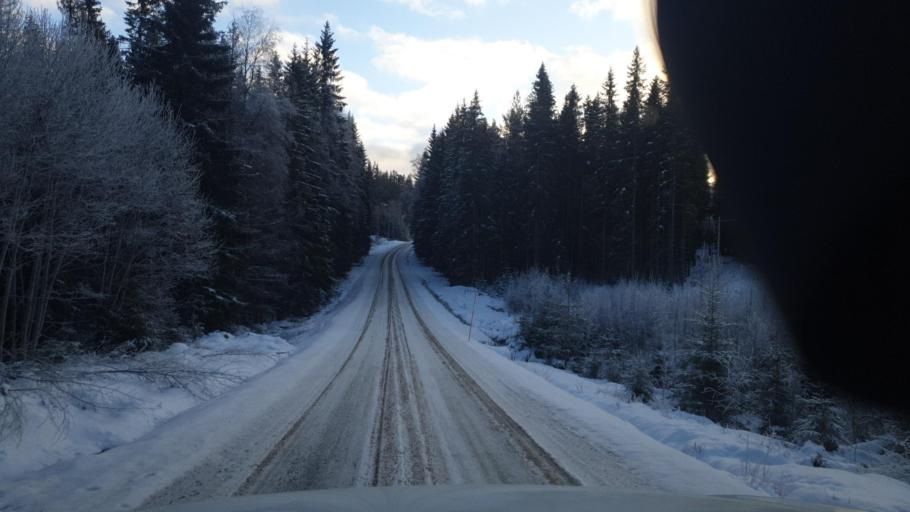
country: SE
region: Vaermland
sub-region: Eda Kommun
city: Charlottenberg
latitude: 60.1466
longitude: 12.5963
